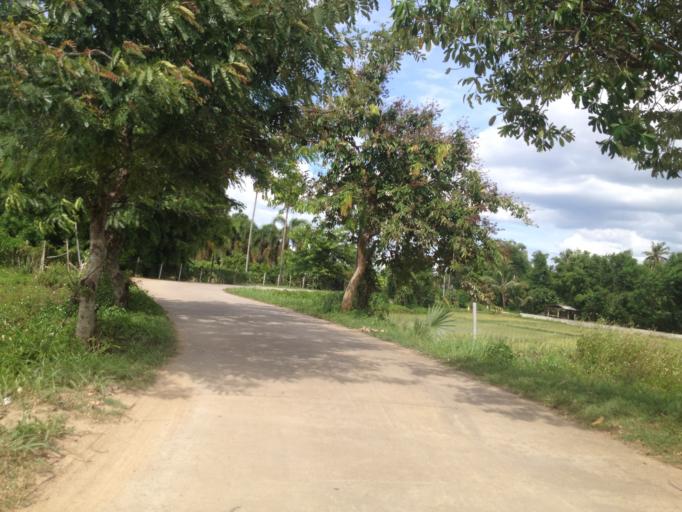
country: TH
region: Chiang Mai
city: Hang Dong
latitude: 18.7134
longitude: 98.9148
